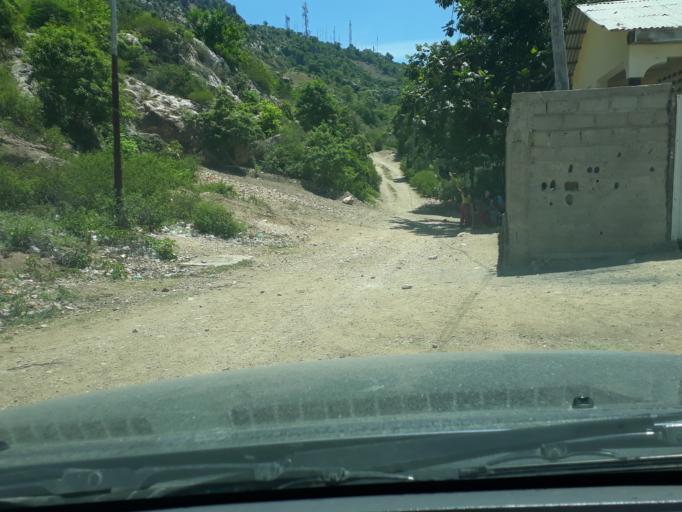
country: HT
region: Nord
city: Okap
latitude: 19.7717
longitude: -72.2071
